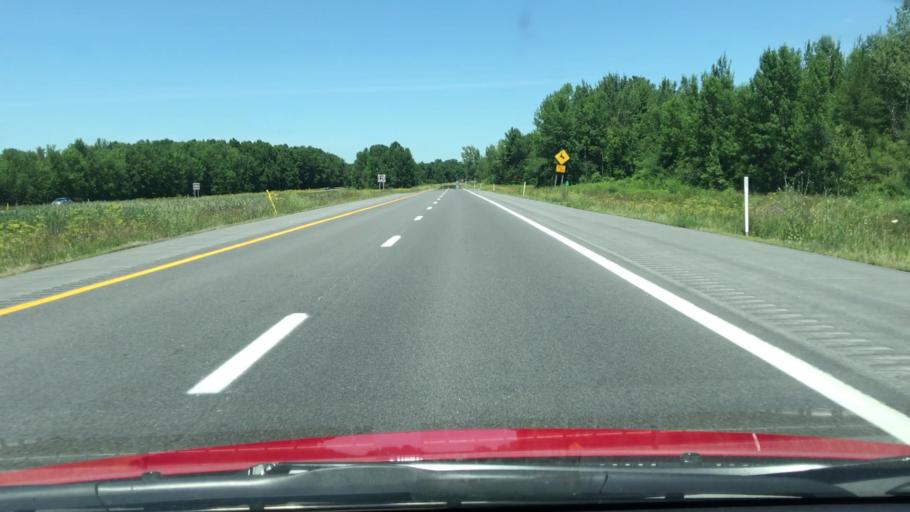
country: US
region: New York
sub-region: Clinton County
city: Cumberland Head
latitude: 44.8460
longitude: -73.4471
